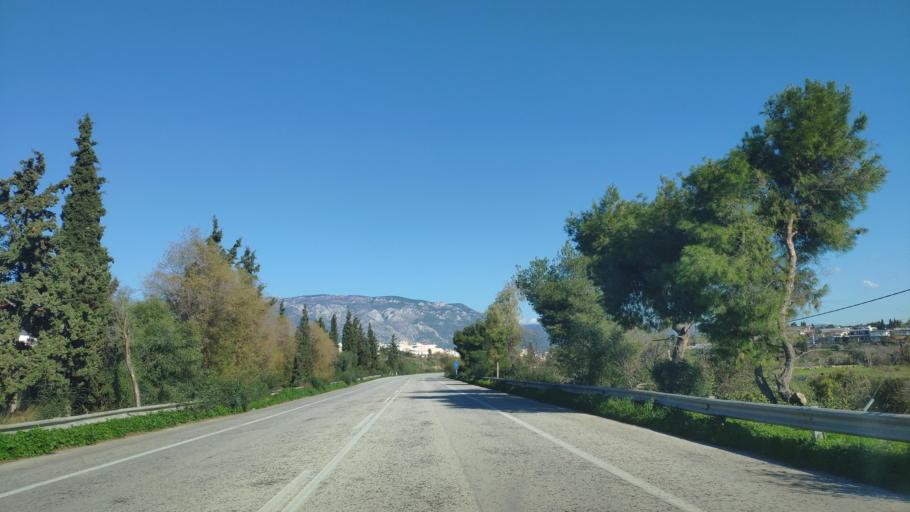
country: GR
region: Peloponnese
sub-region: Nomos Korinthias
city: Examilia
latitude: 37.9284
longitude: 22.9197
